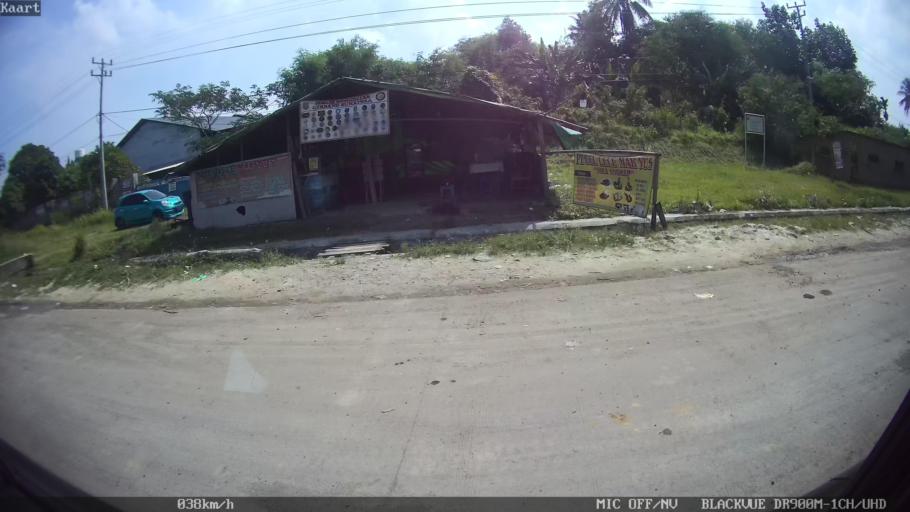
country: ID
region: Lampung
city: Natar
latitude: -5.2814
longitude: 105.1894
